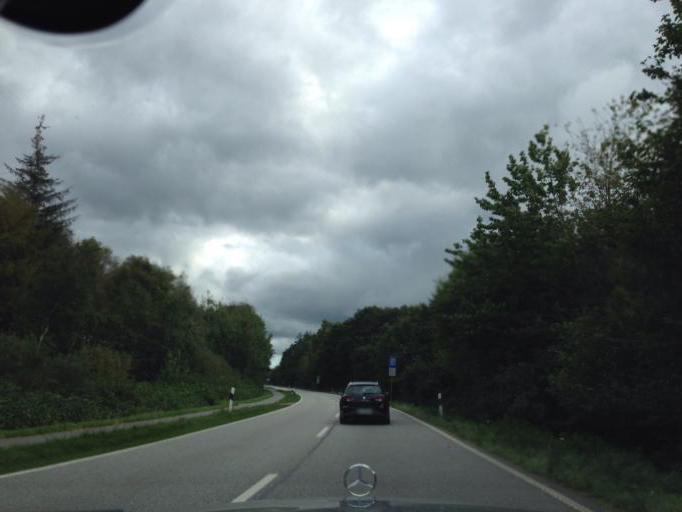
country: DE
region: Schleswig-Holstein
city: Leck
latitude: 54.7599
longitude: 8.9853
